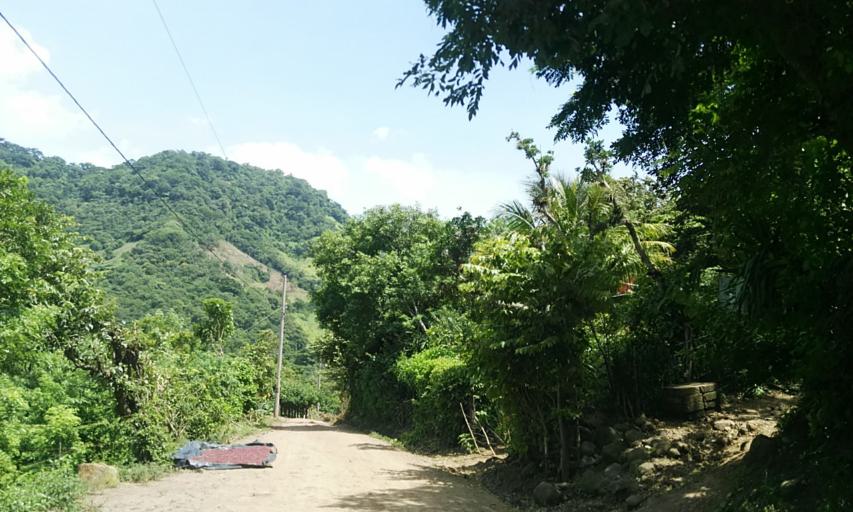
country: NI
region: Matagalpa
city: Terrabona
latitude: 12.7454
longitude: -85.9234
